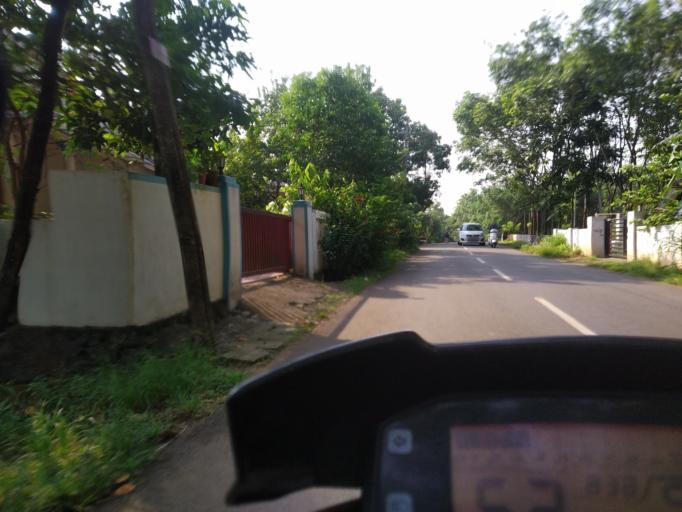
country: IN
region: Kerala
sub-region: Ernakulam
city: Ramamangalam
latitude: 9.9082
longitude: 76.4419
